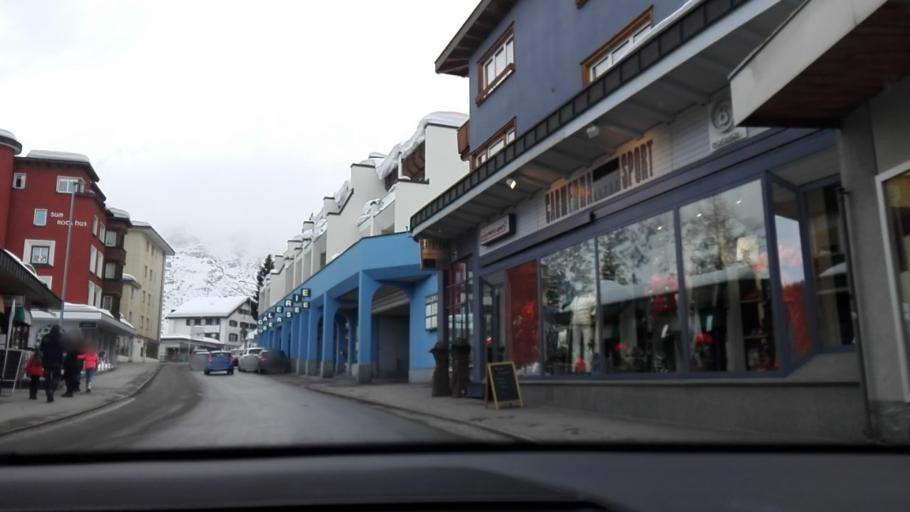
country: CH
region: Grisons
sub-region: Plessur District
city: Arosa
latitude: 46.7820
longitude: 9.6796
